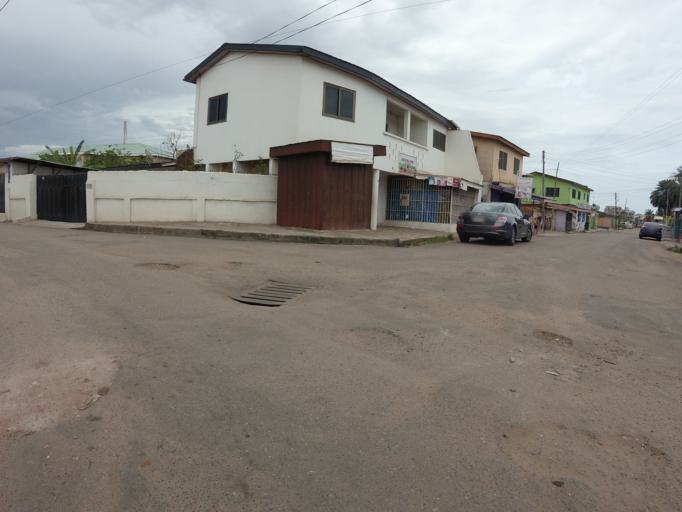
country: GH
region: Greater Accra
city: Accra
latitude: 5.6012
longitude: -0.2152
